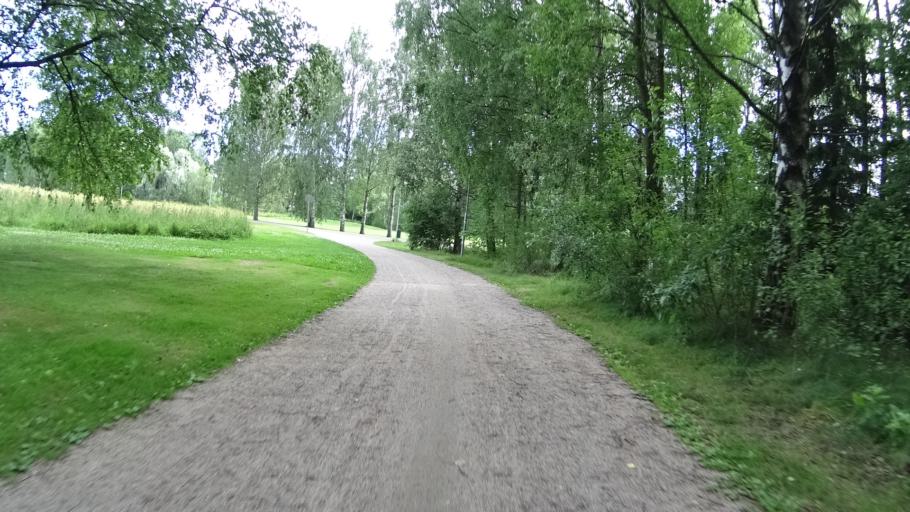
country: FI
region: Uusimaa
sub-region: Helsinki
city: Teekkarikylae
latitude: 60.2015
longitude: 24.8666
